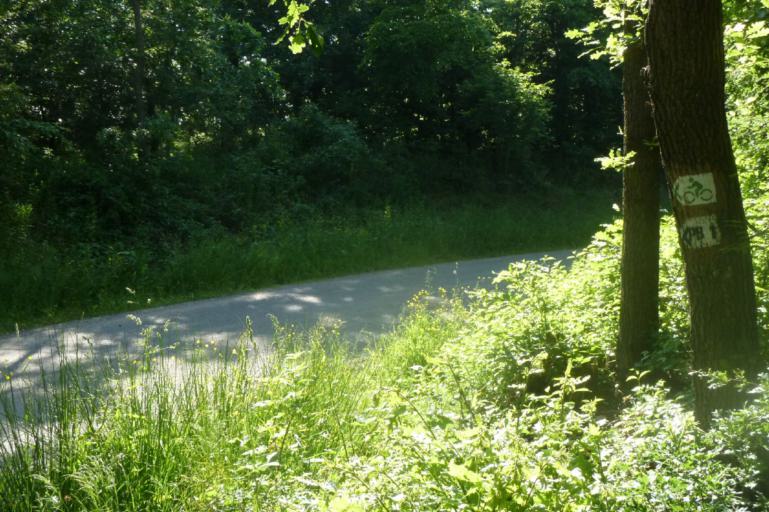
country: HU
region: Pest
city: Pilisszentkereszt
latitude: 47.7042
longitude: 18.9053
